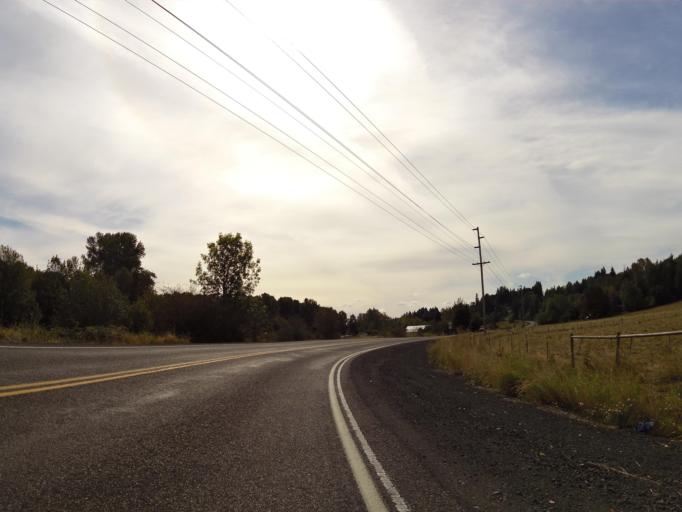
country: US
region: Washington
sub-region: Lewis County
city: Chehalis
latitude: 46.6408
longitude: -122.9716
